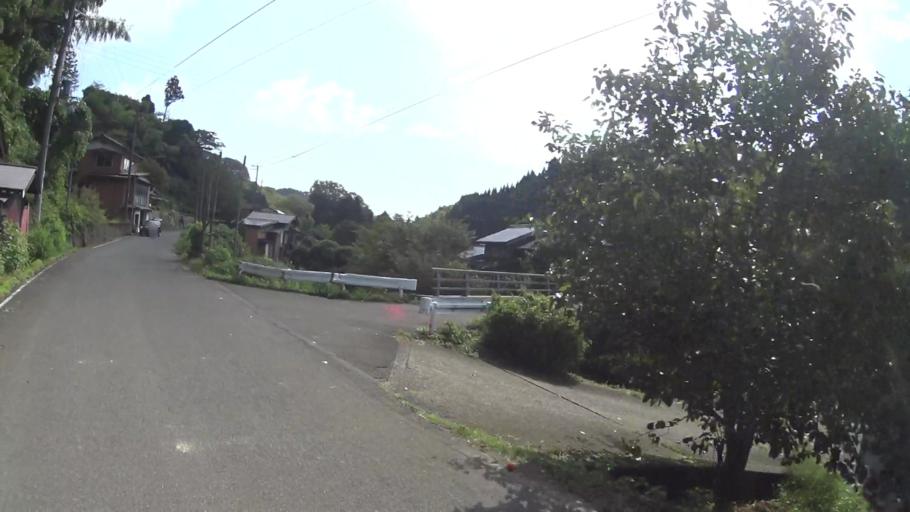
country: JP
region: Kyoto
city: Miyazu
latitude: 35.6719
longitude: 135.2406
